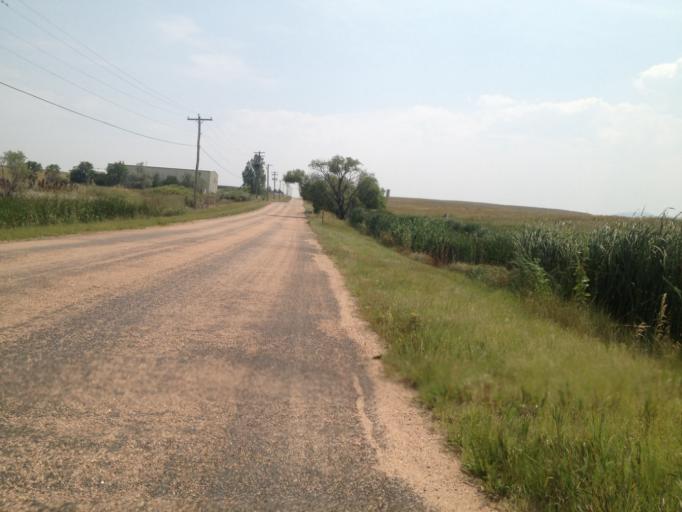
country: US
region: Colorado
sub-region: Boulder County
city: Superior
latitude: 39.9559
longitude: -105.1989
